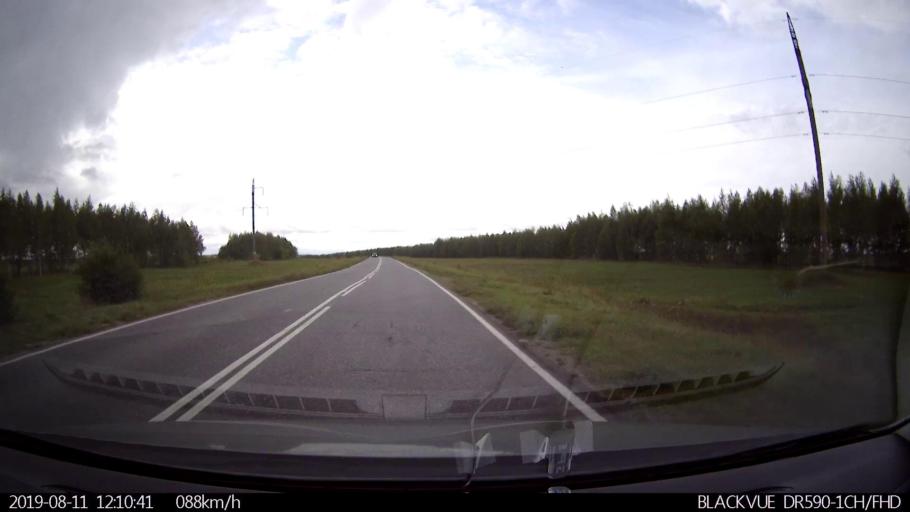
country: RU
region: Ulyanovsk
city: Silikatnyy
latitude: 53.9909
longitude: 48.0181
